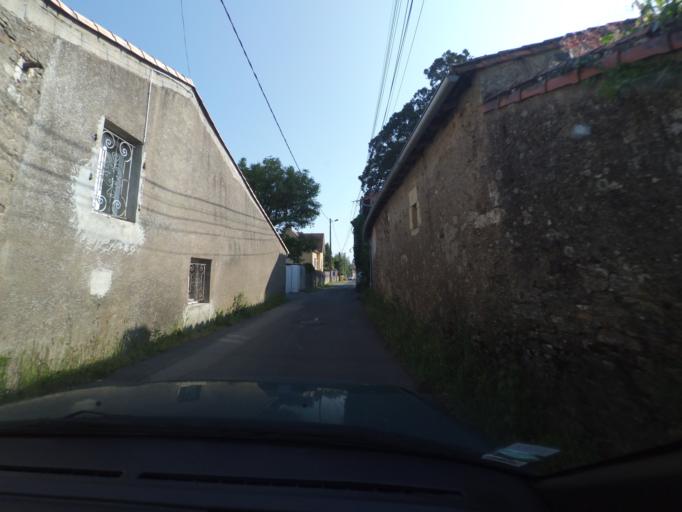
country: FR
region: Pays de la Loire
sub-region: Departement de la Loire-Atlantique
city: Le Pallet
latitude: 47.1377
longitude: -1.3325
